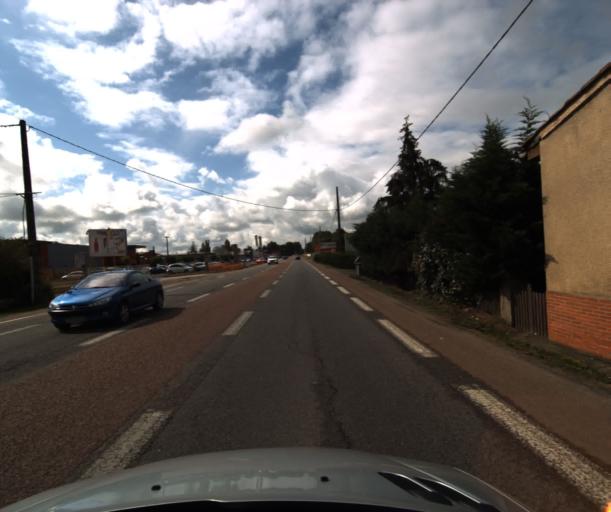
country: FR
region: Midi-Pyrenees
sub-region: Departement du Tarn-et-Garonne
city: Castelsarrasin
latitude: 44.0632
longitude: 1.0973
